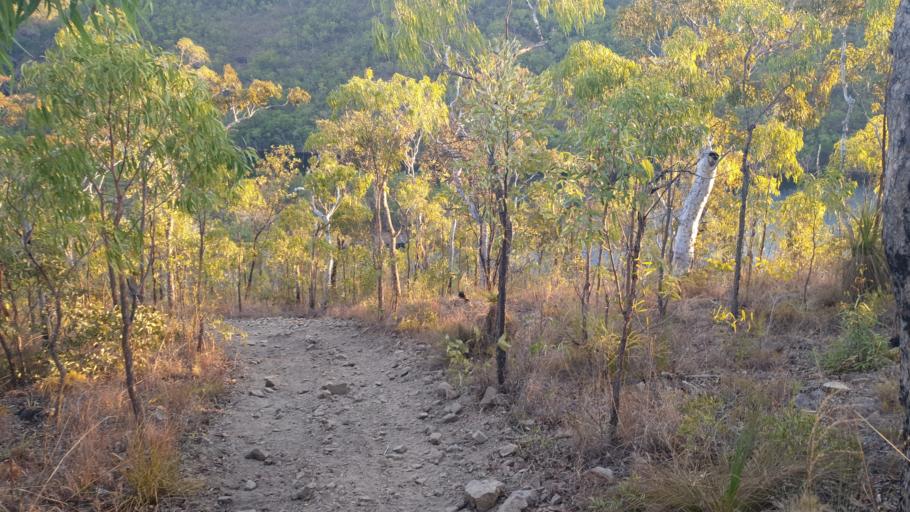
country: AU
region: Queensland
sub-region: Tablelands
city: Atherton
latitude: -17.4025
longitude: 145.2288
